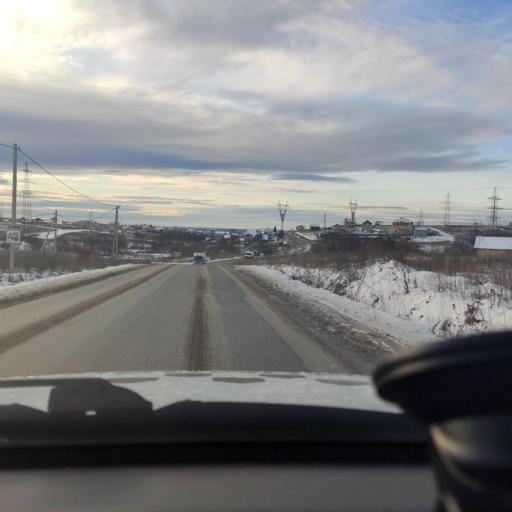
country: RU
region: Perm
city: Ferma
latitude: 57.9528
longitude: 56.3677
